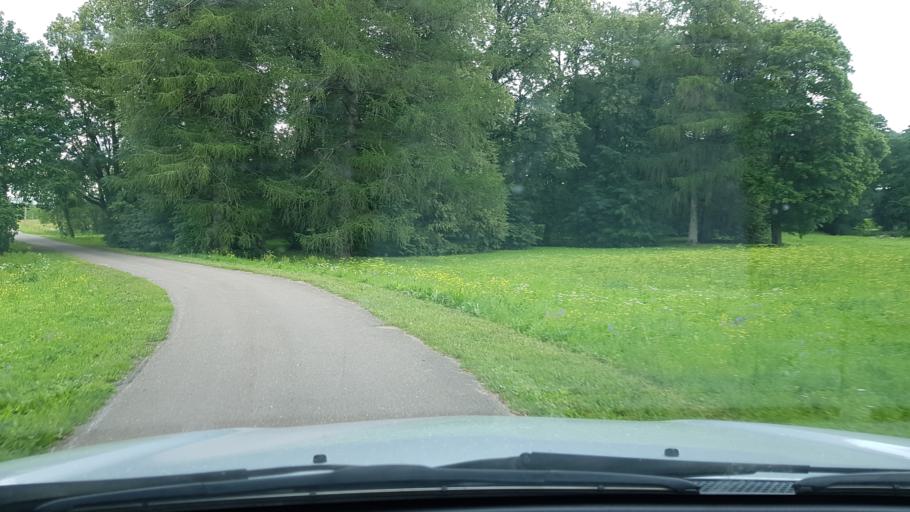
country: EE
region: Ida-Virumaa
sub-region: Narva-Joesuu linn
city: Narva-Joesuu
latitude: 59.3881
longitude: 27.9811
